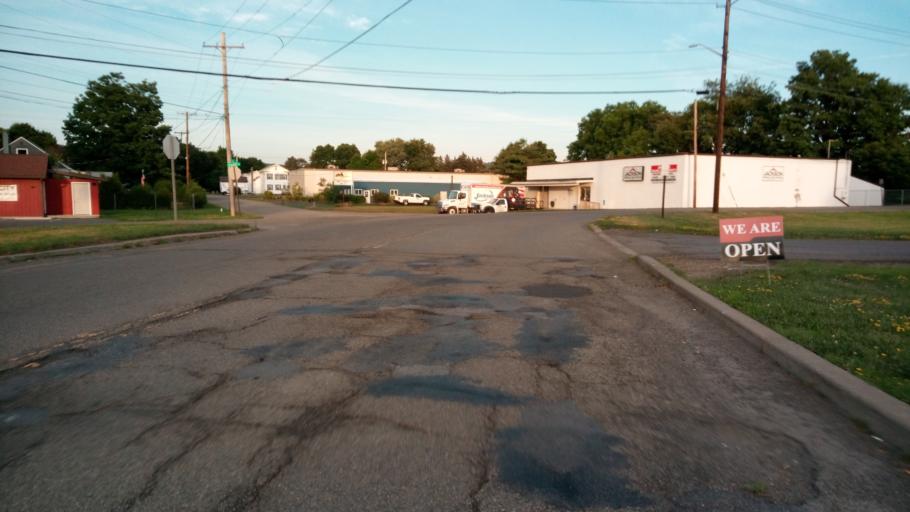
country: US
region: New York
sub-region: Chemung County
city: Horseheads
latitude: 42.1580
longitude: -76.8360
